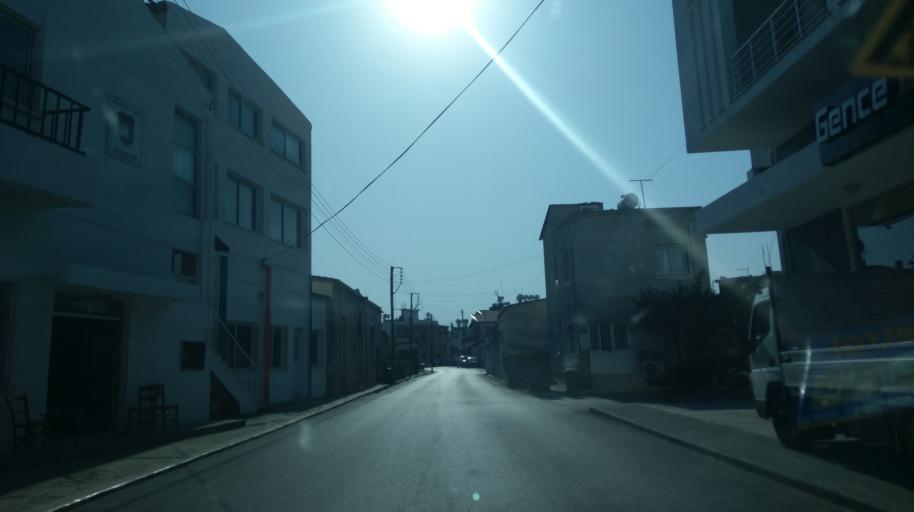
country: CY
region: Lefkosia
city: Morfou
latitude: 35.1997
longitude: 32.9899
